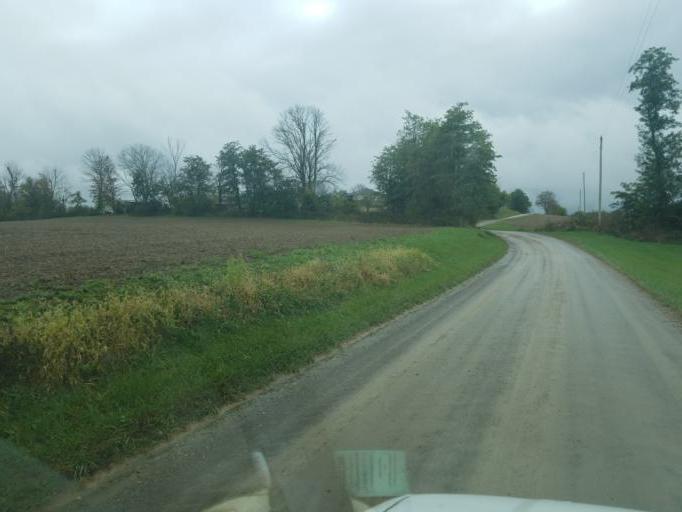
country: US
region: Ohio
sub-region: Holmes County
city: Millersburg
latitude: 40.5830
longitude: -81.9947
